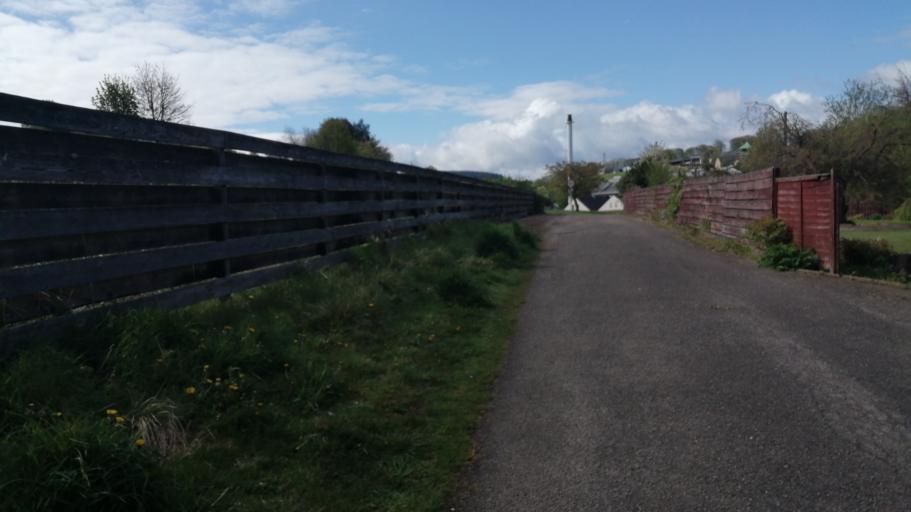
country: GB
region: Scotland
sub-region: Moray
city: Keith
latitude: 57.5408
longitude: -2.9599
